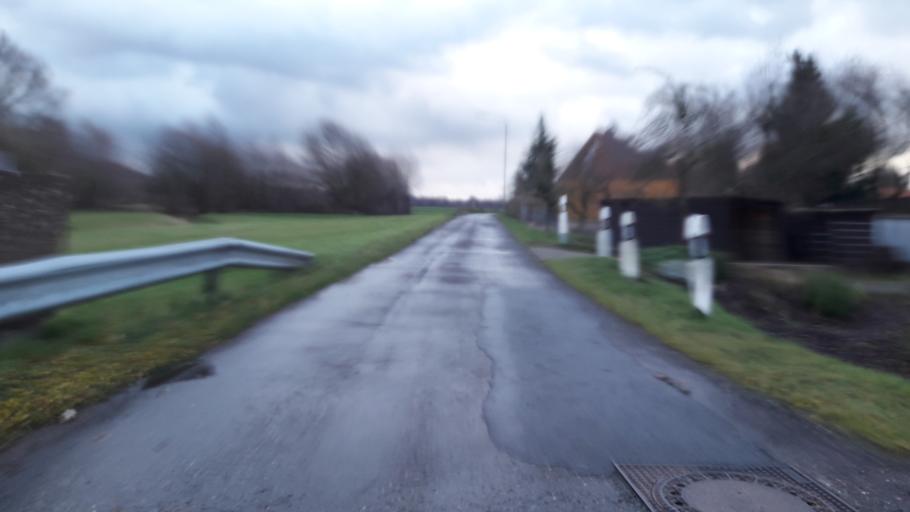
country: DE
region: North Rhine-Westphalia
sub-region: Regierungsbezirk Detmold
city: Petershagen
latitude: 52.3271
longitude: 8.9683
